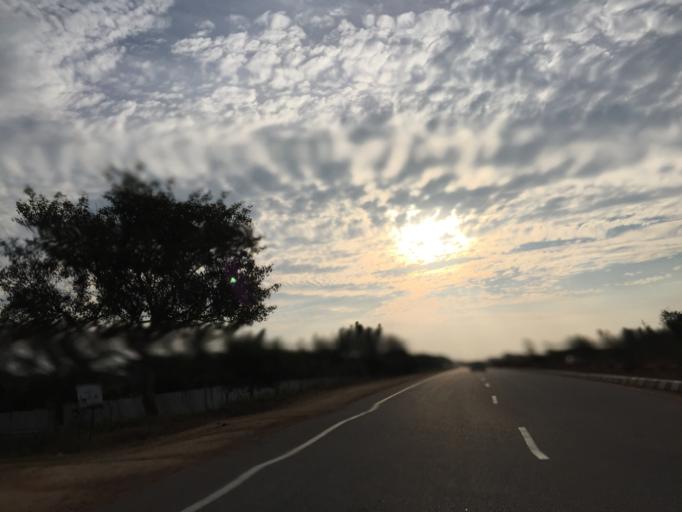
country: IN
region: Karnataka
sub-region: Kolar
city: Kolar
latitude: 13.1445
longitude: 78.2403
